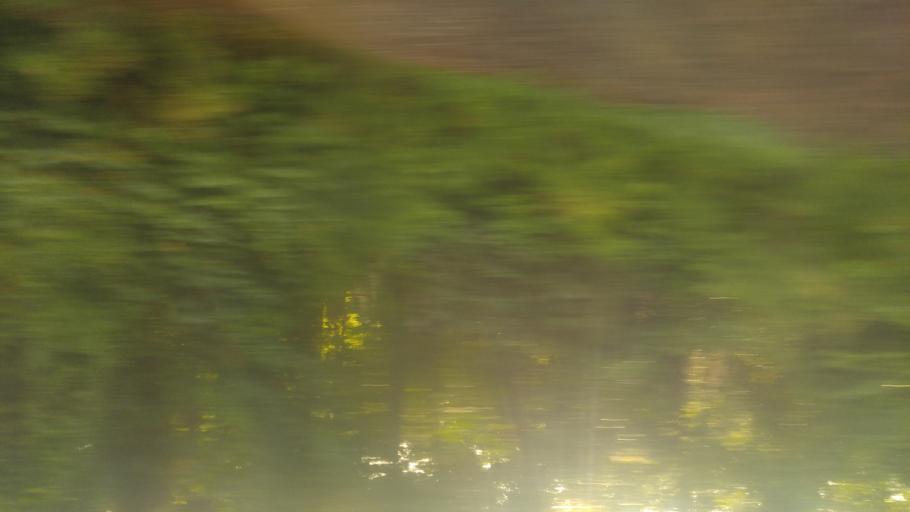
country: US
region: North Carolina
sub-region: Wake County
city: Raleigh
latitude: 35.7425
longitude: -78.6382
